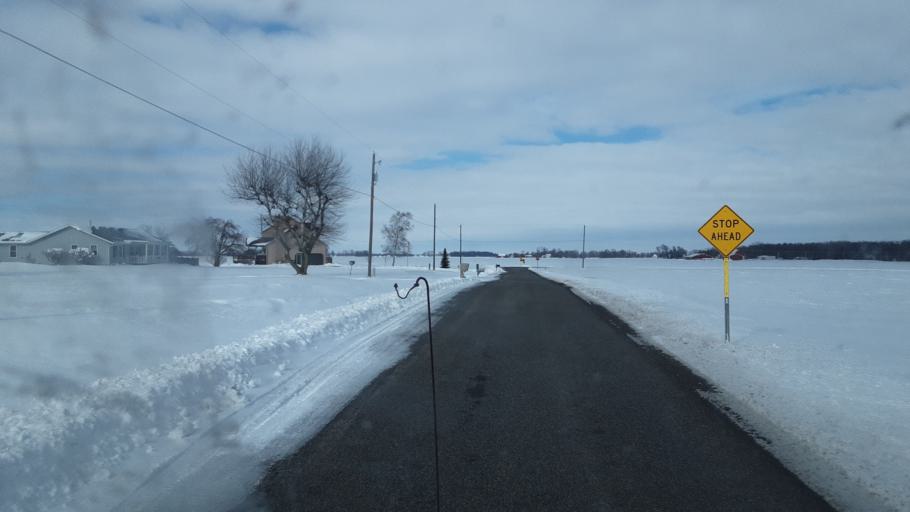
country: US
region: Ohio
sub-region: Delaware County
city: Delaware
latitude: 40.2853
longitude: -82.9914
